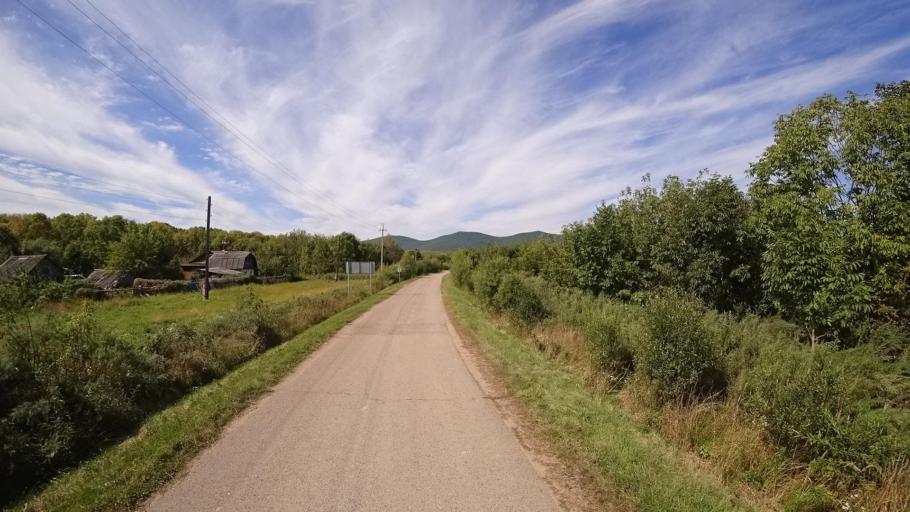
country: RU
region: Primorskiy
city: Kirovskiy
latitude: 44.7592
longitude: 133.6109
